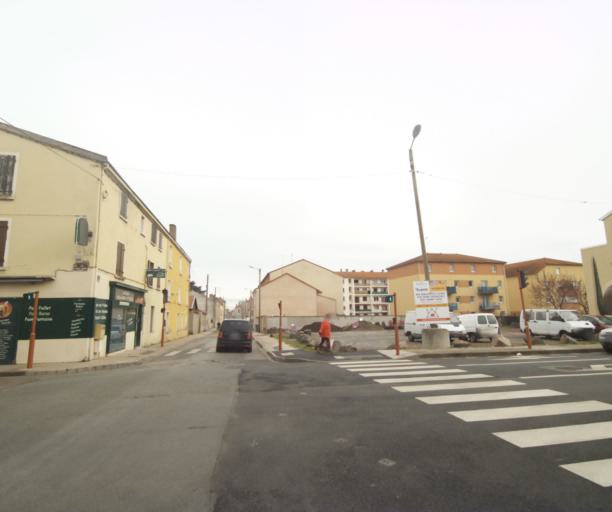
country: FR
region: Rhone-Alpes
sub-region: Departement de la Loire
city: Riorges
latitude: 46.0357
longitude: 4.0520
